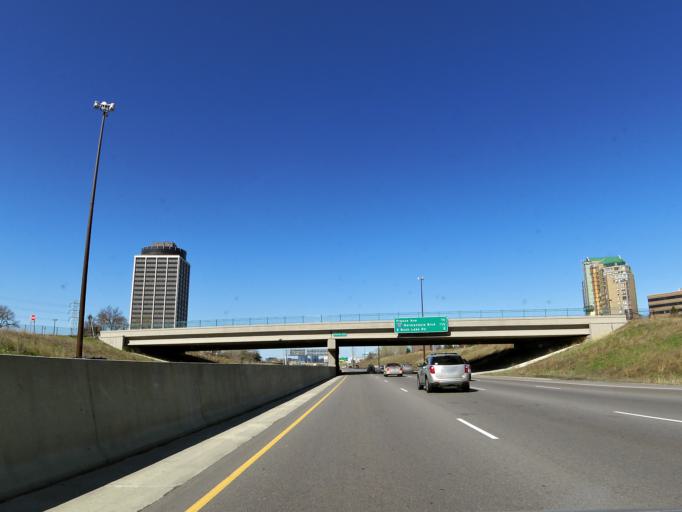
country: US
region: Minnesota
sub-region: Hennepin County
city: Bloomington
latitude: 44.8615
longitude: -93.3175
